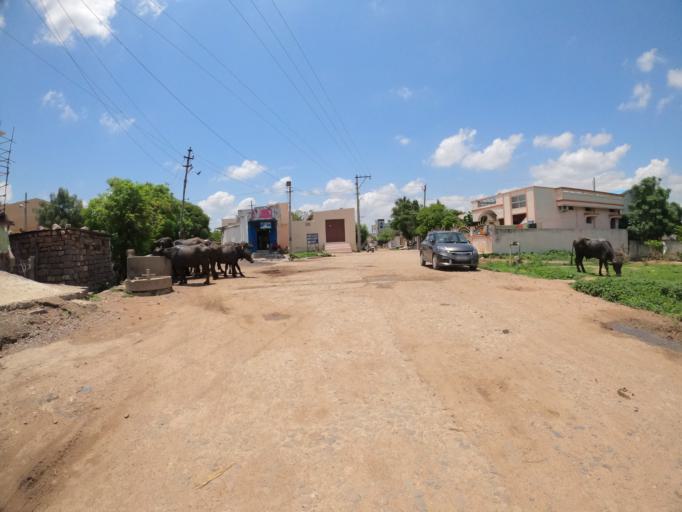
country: IN
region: Telangana
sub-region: Rangareddi
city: Singapur
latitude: 17.4396
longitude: 78.1599
